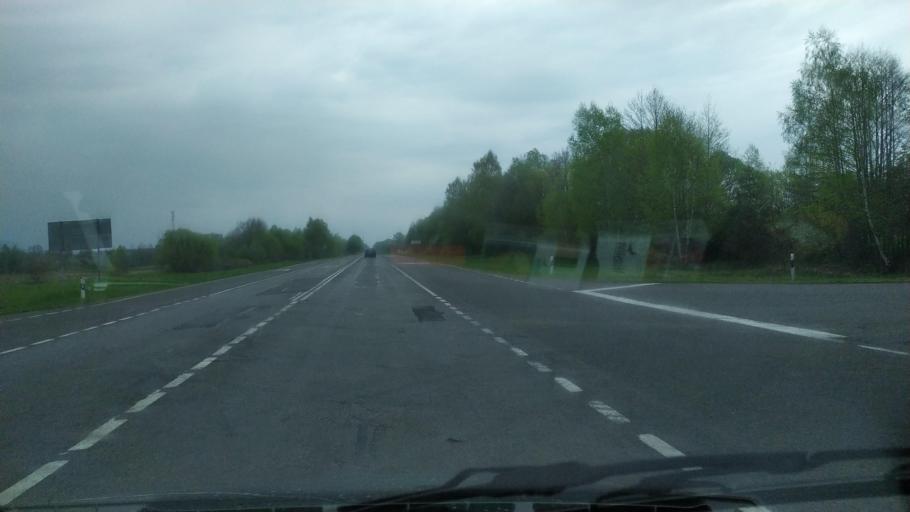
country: BY
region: Brest
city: Horad Kobryn
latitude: 52.3244
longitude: 24.5671
